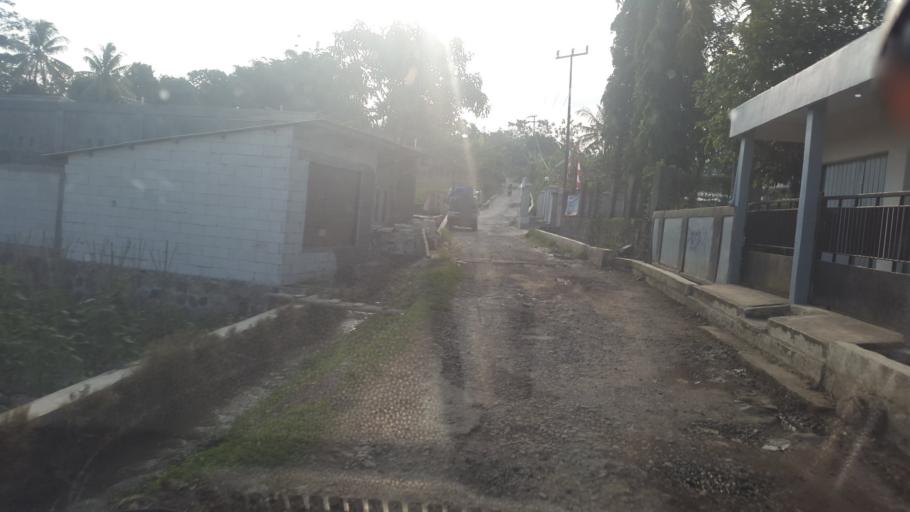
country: ID
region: West Java
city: Cicurug
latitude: -6.8183
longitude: 106.7464
